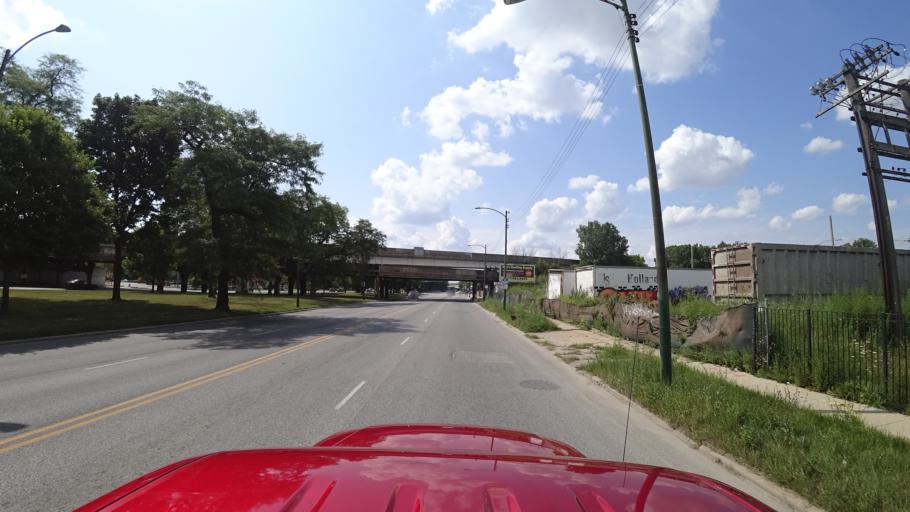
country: US
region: Illinois
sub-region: Cook County
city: Chicago
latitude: 41.8279
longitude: -87.6850
